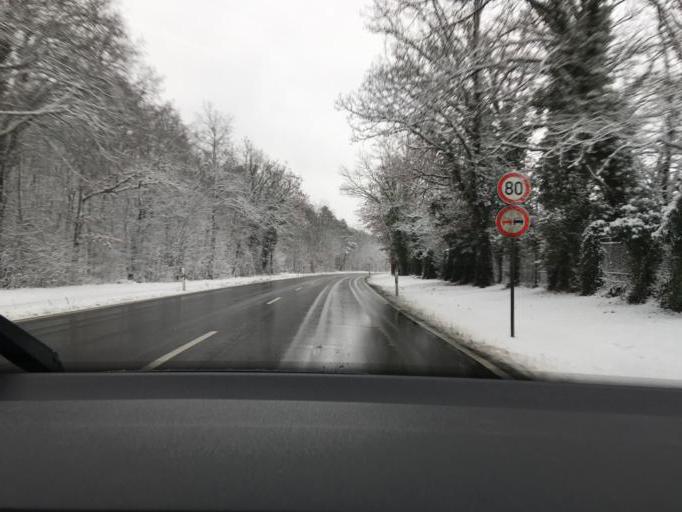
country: DE
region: Baden-Wuerttemberg
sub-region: Freiburg Region
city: Singen
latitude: 47.7643
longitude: 8.8650
